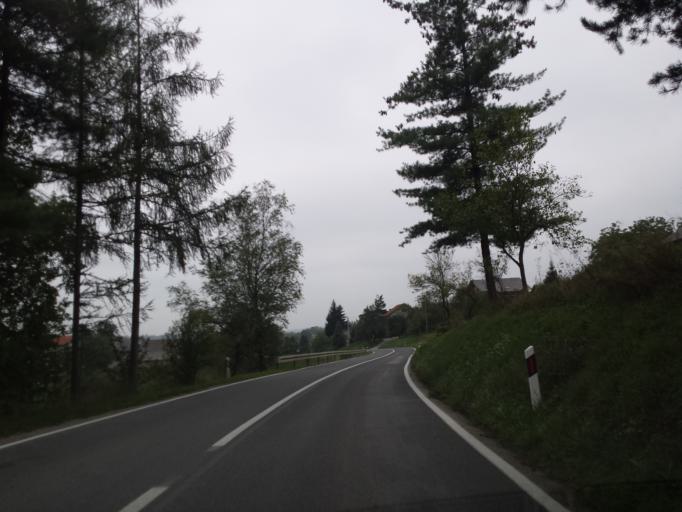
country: HR
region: Karlovacka
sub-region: Grad Karlovac
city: Karlovac
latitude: 45.4150
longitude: 15.4554
